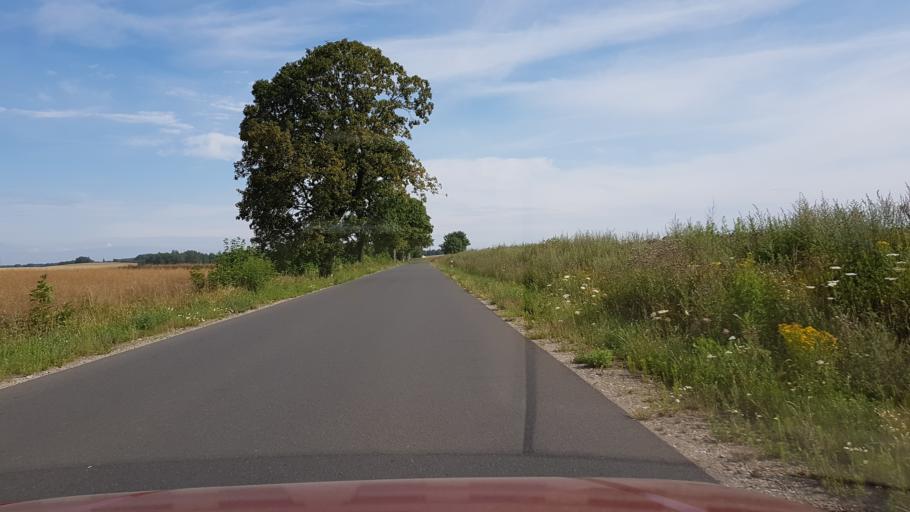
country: PL
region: West Pomeranian Voivodeship
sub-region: Powiat koszalinski
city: Polanow
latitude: 54.1421
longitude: 16.6215
